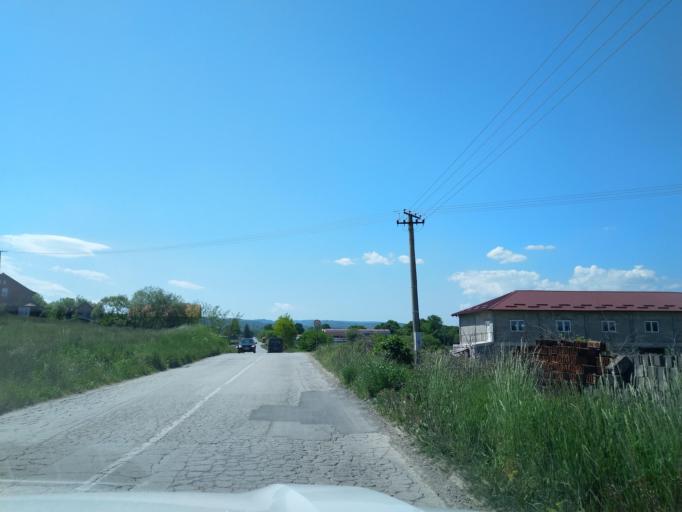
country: RS
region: Central Serbia
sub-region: Zlatiborski Okrug
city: Pozega
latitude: 43.8522
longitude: 19.9995
